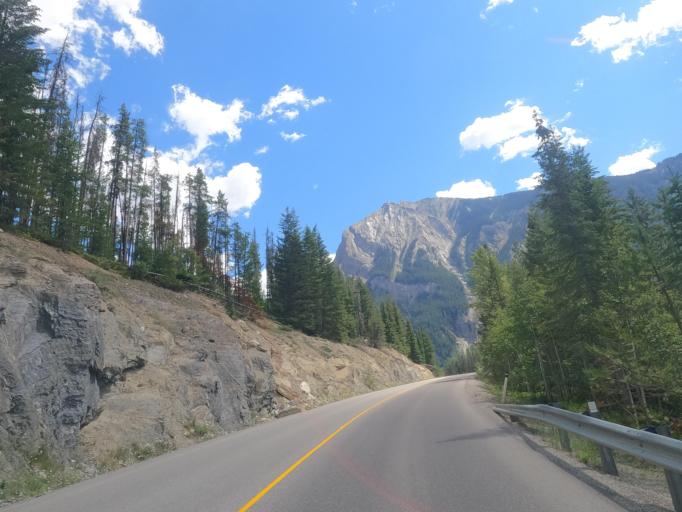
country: CA
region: Alberta
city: Lake Louise
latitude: 51.3806
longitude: -116.5211
